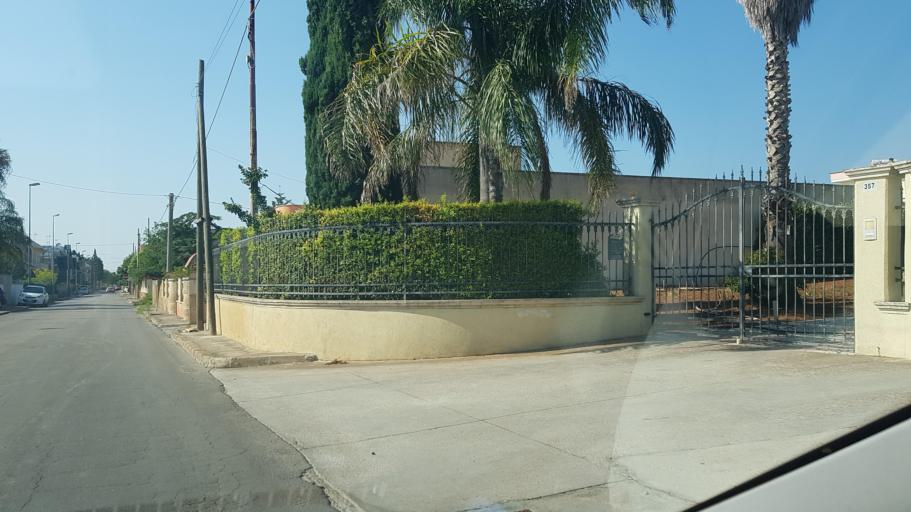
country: IT
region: Apulia
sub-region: Provincia di Lecce
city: Taurisano
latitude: 39.9488
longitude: 18.2191
